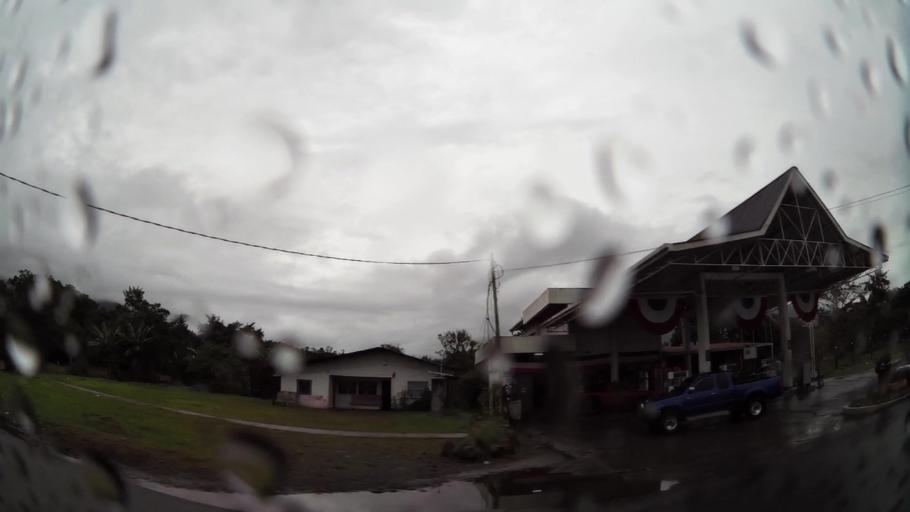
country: PA
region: Chiriqui
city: Volcan
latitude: 8.7840
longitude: -82.6488
